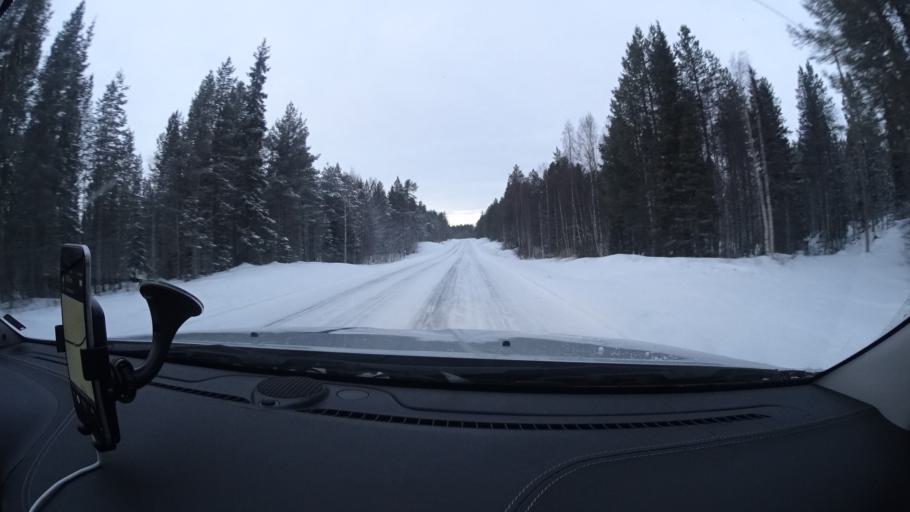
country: FI
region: Lapland
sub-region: Itae-Lappi
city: Posio
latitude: 66.0928
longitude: 28.6598
